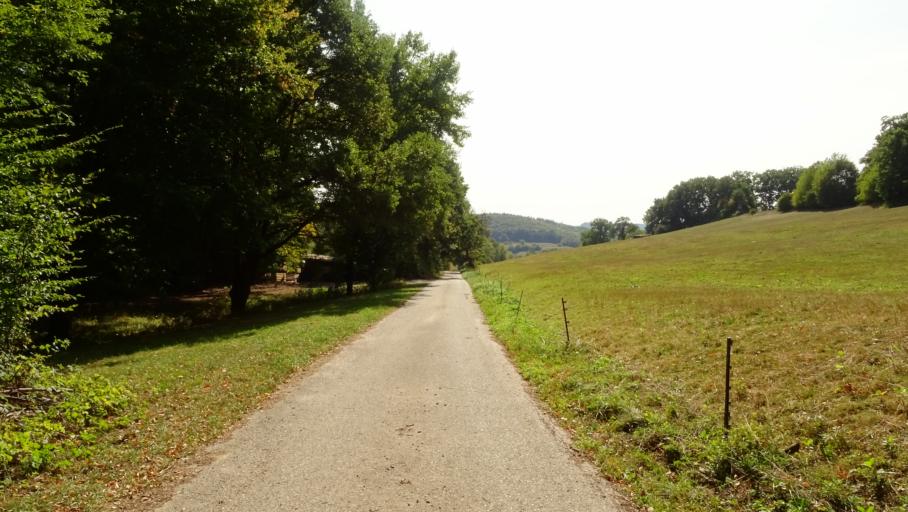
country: DE
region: Baden-Wuerttemberg
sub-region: Karlsruhe Region
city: Mosbach
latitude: 49.3855
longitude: 9.1644
